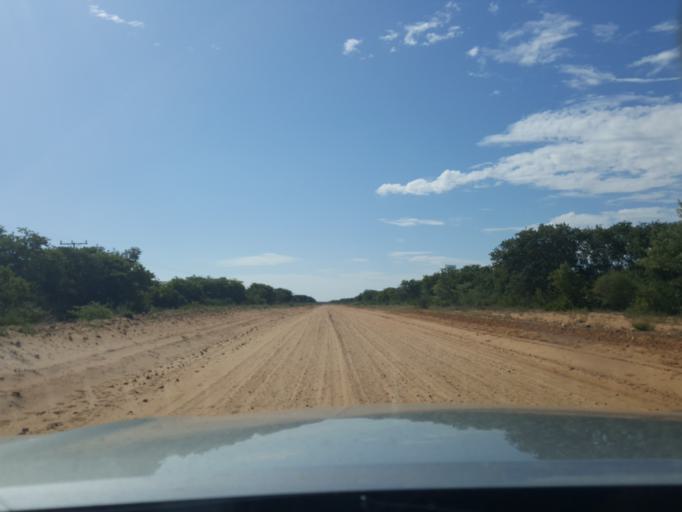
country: BW
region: Kweneng
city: Khudumelapye
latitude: -23.7175
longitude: 24.7345
